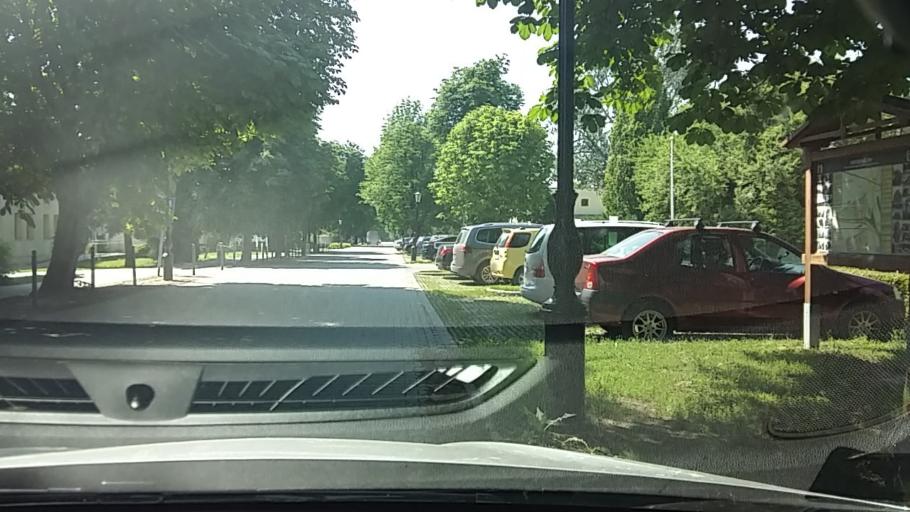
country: HU
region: Fejer
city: Etyek
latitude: 47.5020
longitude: 18.7519
